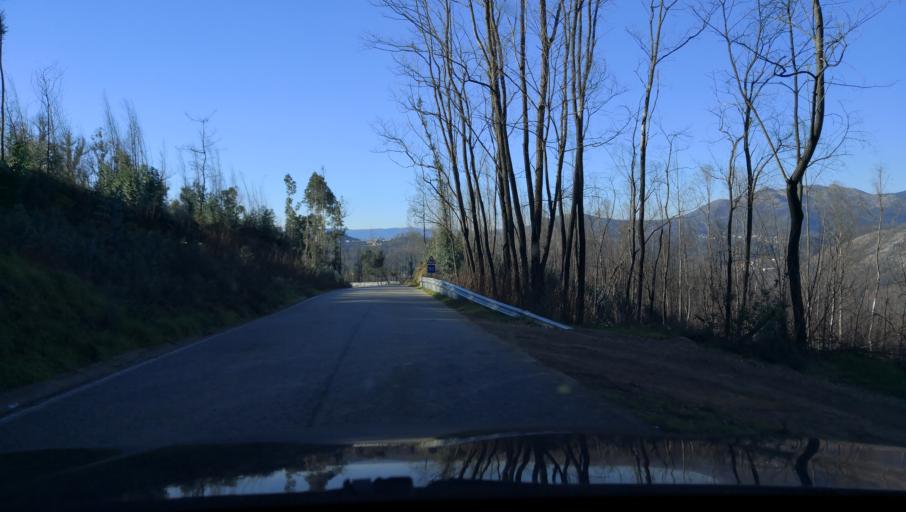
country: PT
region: Viseu
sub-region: Vouzela
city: Vouzela
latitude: 40.7306
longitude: -8.1426
